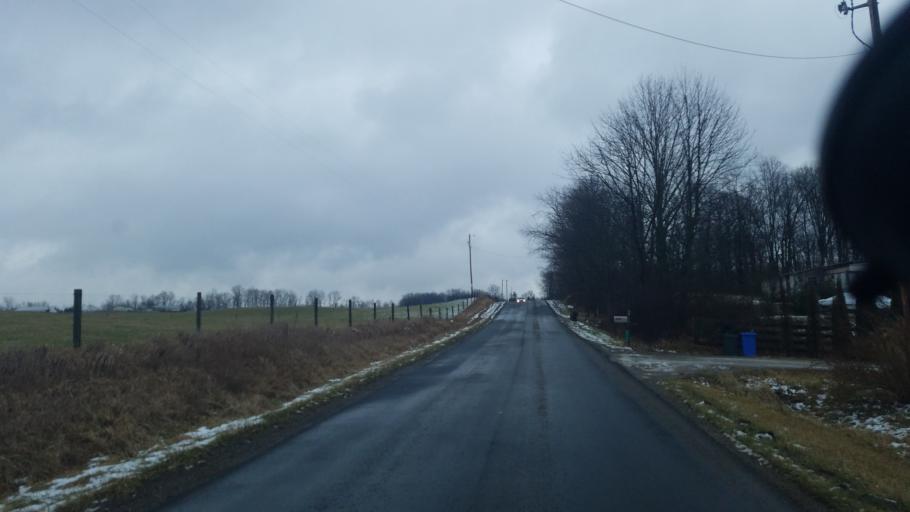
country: US
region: Ohio
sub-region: Morrow County
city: Mount Gilead
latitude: 40.5035
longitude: -82.6902
